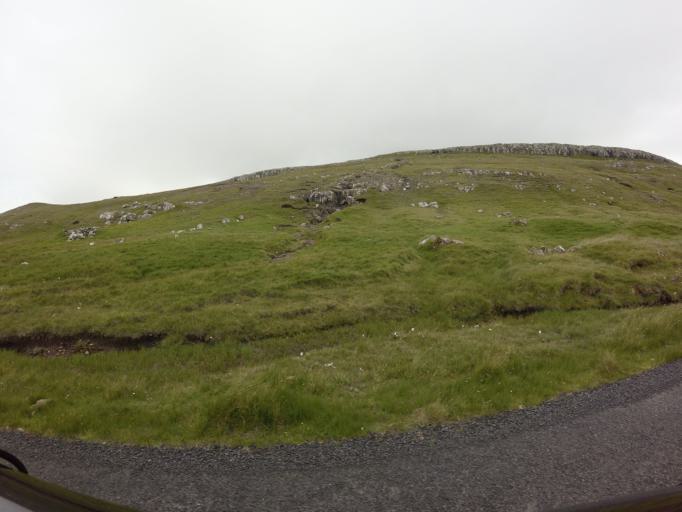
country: FO
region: Sandoy
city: Sandur
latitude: 61.8155
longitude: -6.7477
